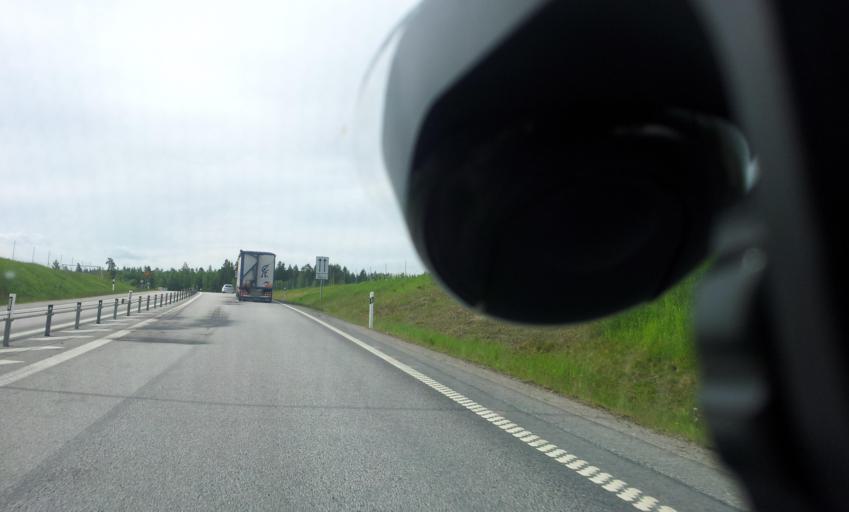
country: SE
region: OEstergoetland
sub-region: Soderkopings Kommun
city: Soederkoeping
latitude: 58.4526
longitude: 16.3655
